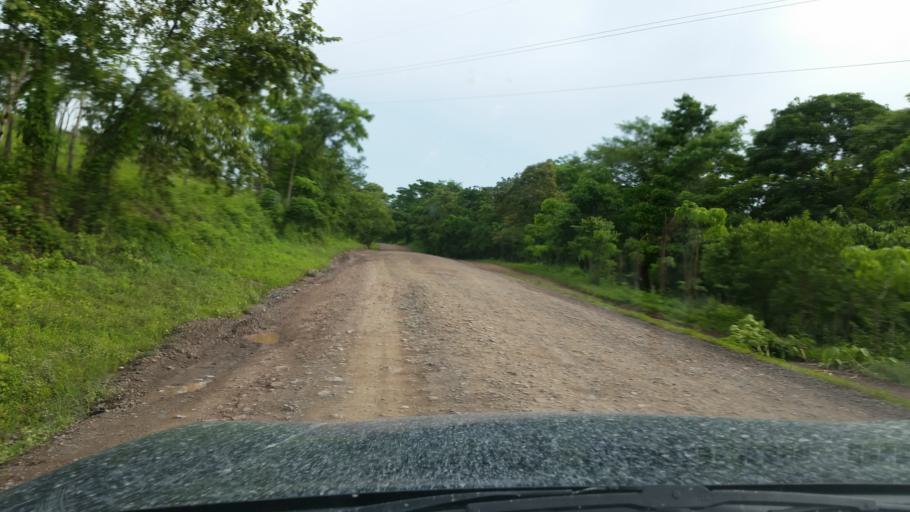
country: NI
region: Atlantico Norte (RAAN)
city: Siuna
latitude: 13.4674
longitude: -84.8470
